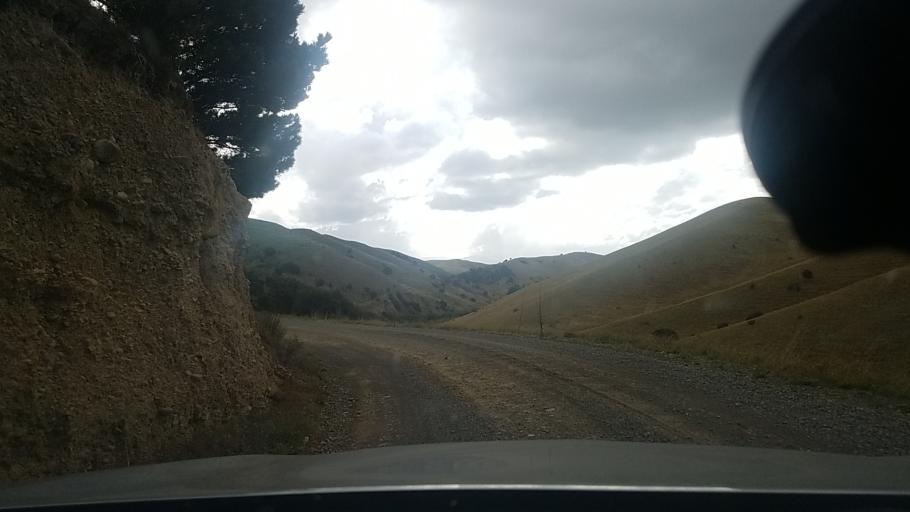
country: NZ
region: Marlborough
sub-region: Marlborough District
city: Blenheim
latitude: -41.5864
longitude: 174.0710
